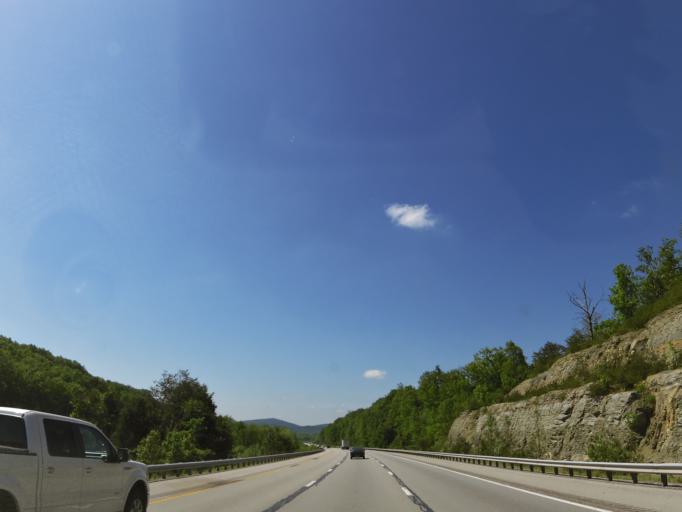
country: US
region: Kentucky
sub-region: Madison County
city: Berea
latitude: 37.5342
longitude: -84.3211
